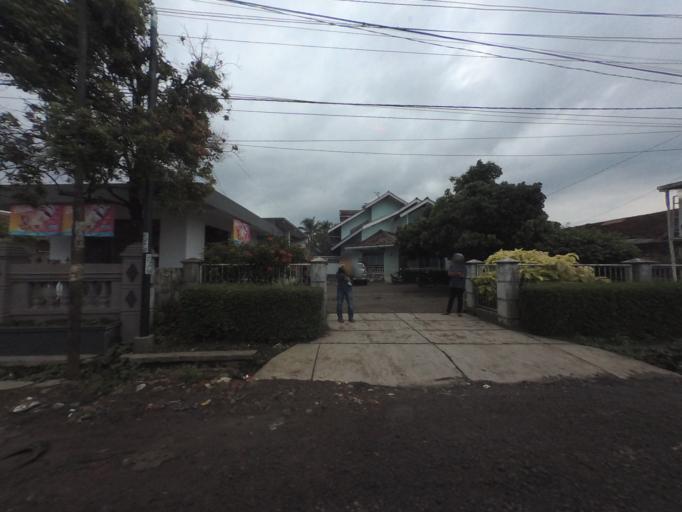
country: ID
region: West Java
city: Cicurug
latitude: -6.8384
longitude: 106.7608
